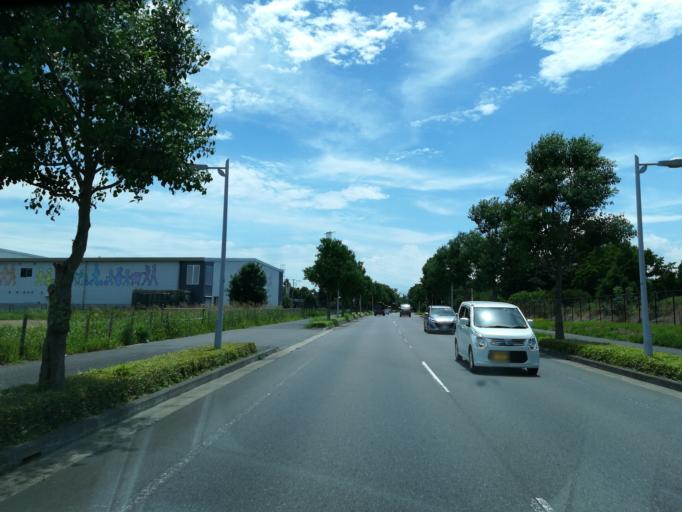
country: JP
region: Ibaraki
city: Naka
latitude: 36.0752
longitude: 140.0796
